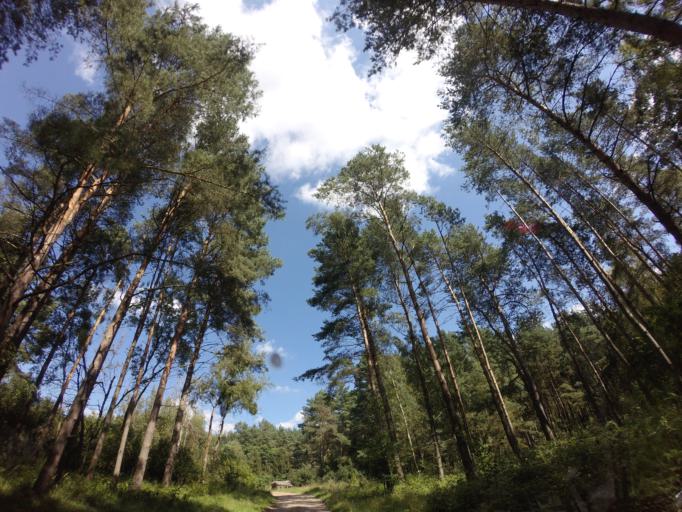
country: PL
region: West Pomeranian Voivodeship
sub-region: Powiat choszczenski
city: Drawno
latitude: 53.2425
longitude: 15.6662
